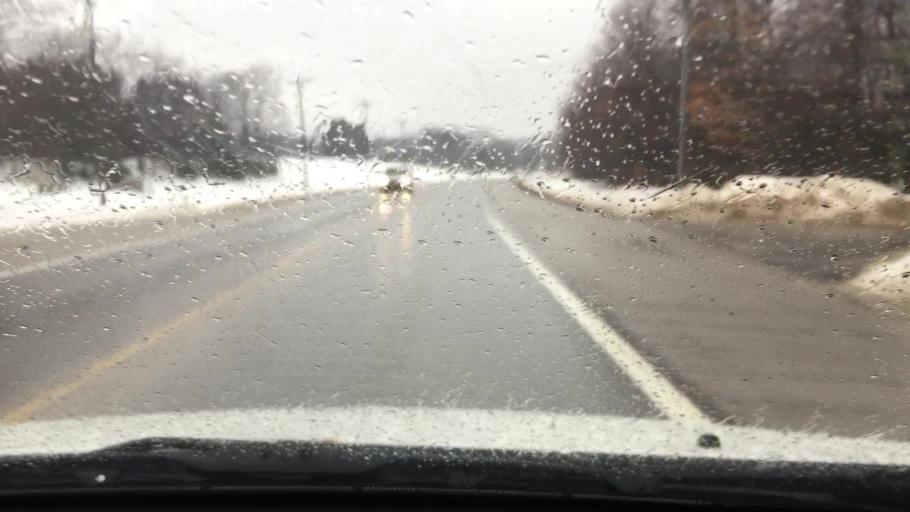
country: US
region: Michigan
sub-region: Charlevoix County
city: Charlevoix
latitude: 45.2825
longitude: -85.2383
